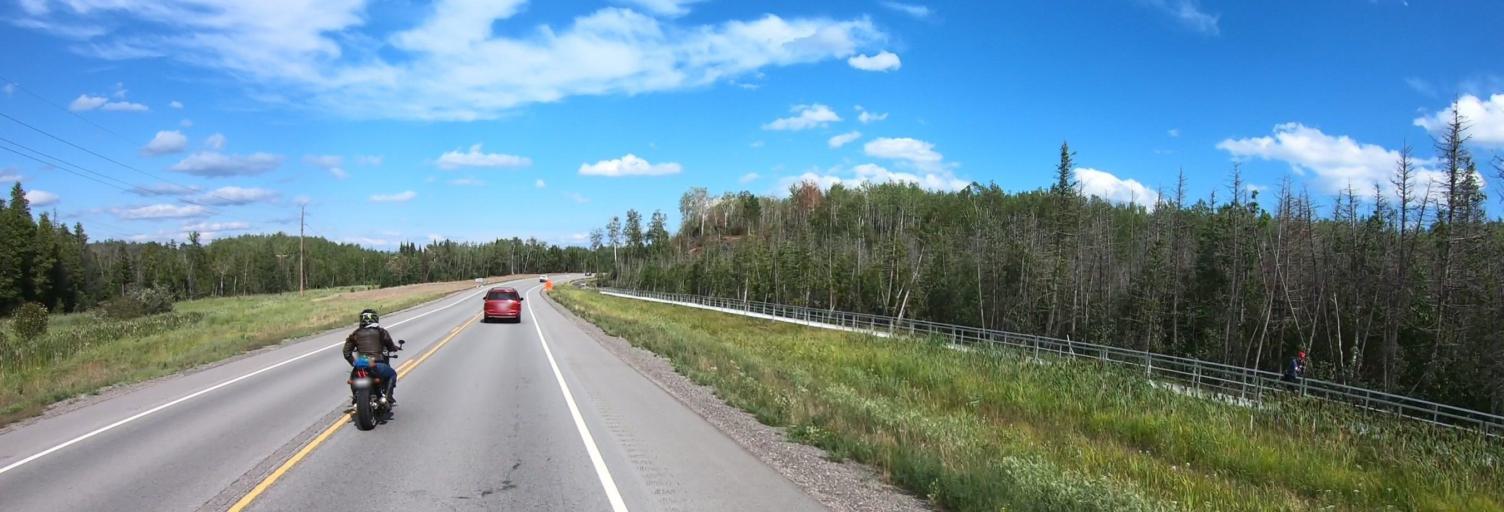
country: US
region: Minnesota
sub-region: Saint Louis County
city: Babbitt
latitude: 47.8475
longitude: -92.1154
